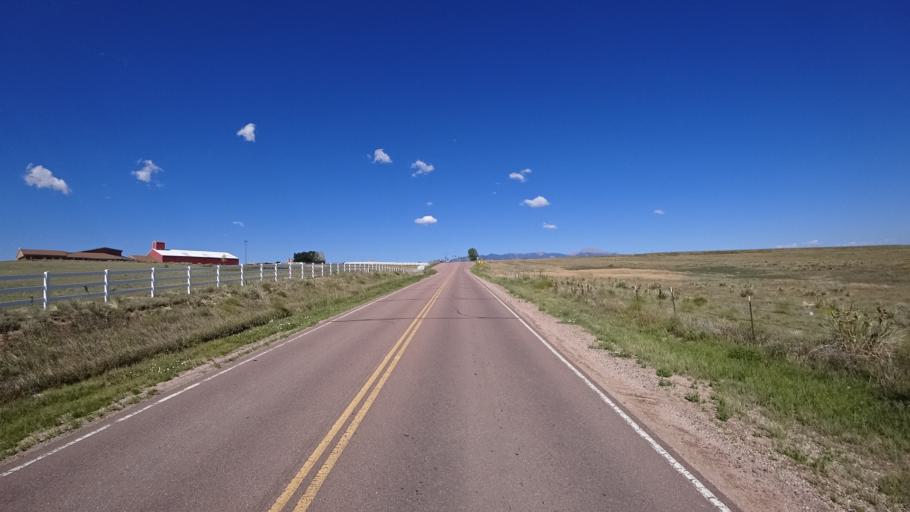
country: US
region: Colorado
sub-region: El Paso County
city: Security-Widefield
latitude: 38.7375
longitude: -104.6787
